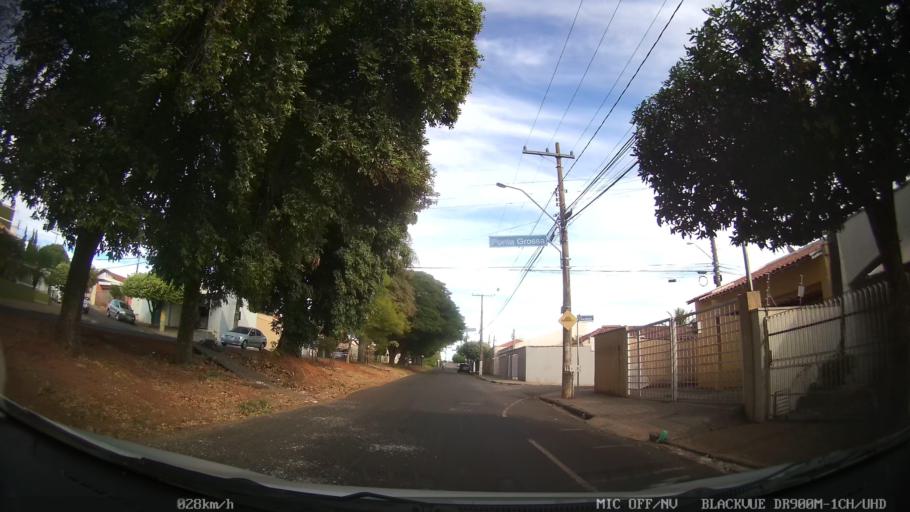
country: BR
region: Sao Paulo
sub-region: Catanduva
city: Catanduva
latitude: -21.1373
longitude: -48.9923
